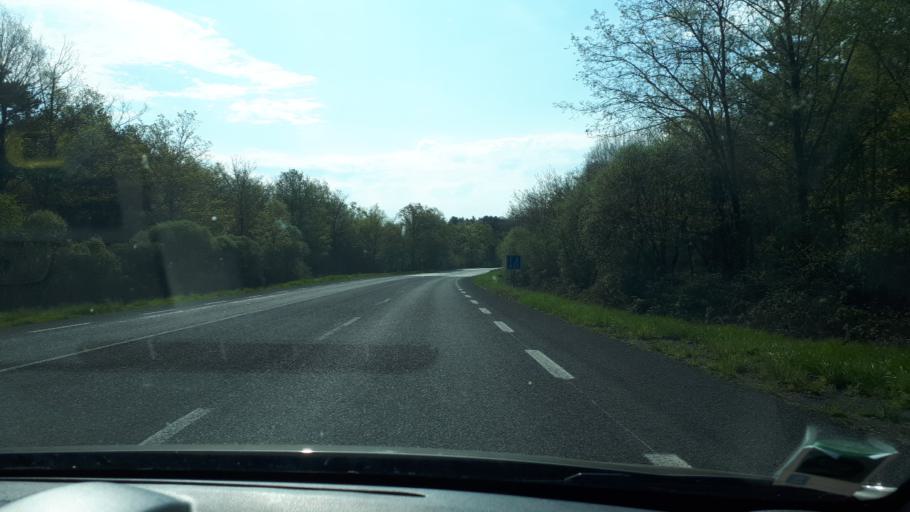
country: FR
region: Centre
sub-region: Departement du Loir-et-Cher
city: Mur-de-Sologne
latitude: 47.3936
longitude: 1.6493
